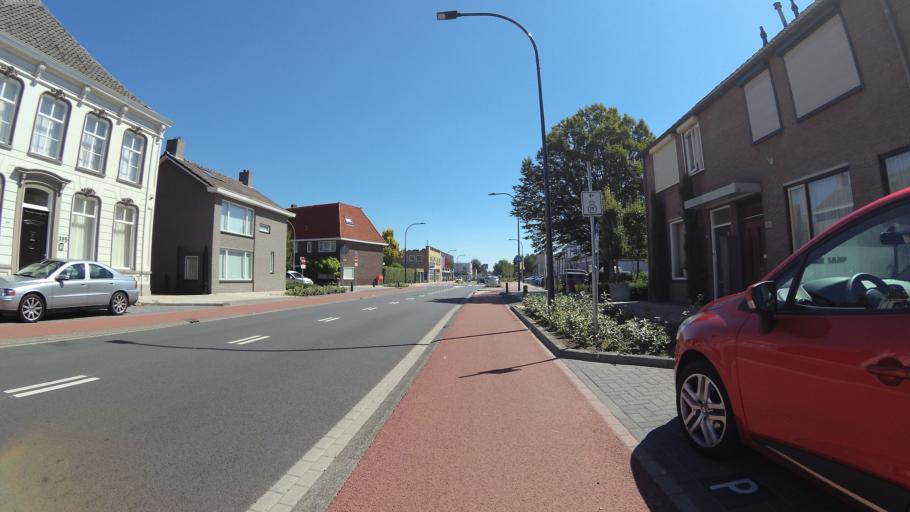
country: NL
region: North Brabant
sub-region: Gemeente Waalwijk
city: Waalwijk
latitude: 51.6913
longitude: 5.0762
